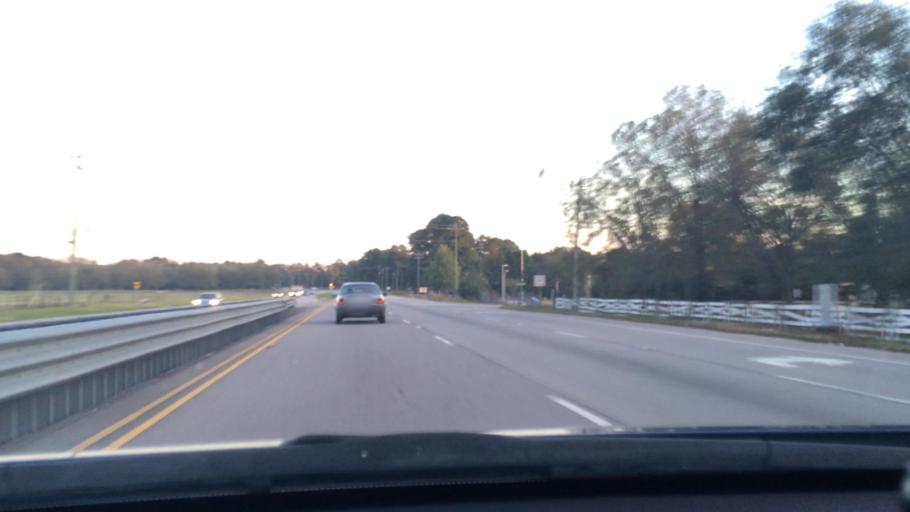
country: US
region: South Carolina
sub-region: Richland County
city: Hopkins
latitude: 33.9447
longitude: -80.8062
